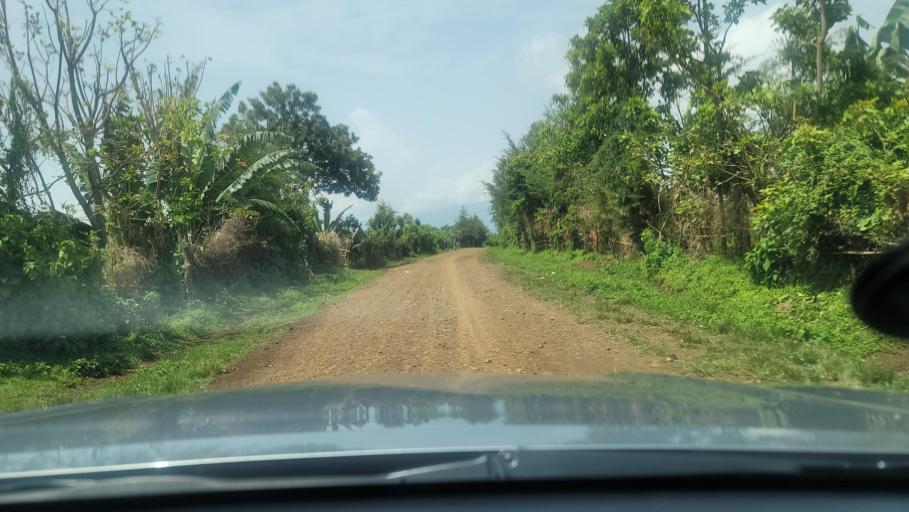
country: ET
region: Oromiya
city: Agaro
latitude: 7.8308
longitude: 36.4068
